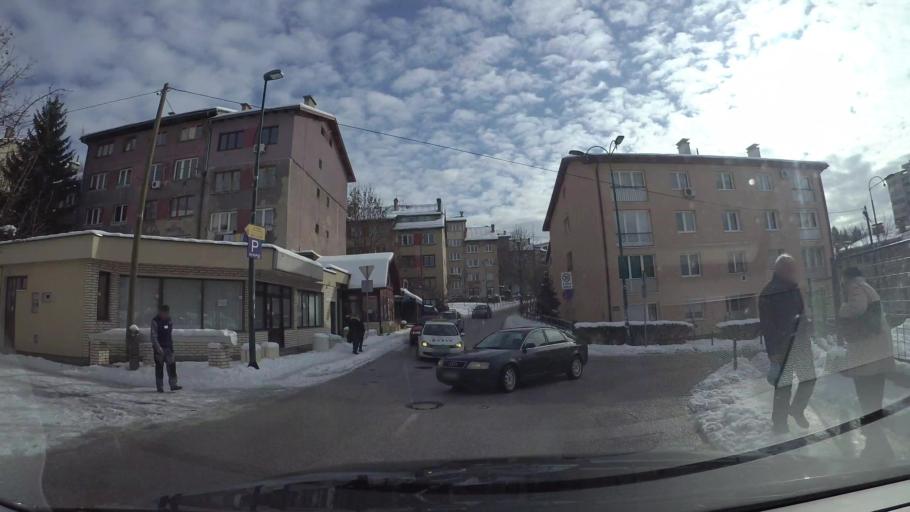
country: BA
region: Federation of Bosnia and Herzegovina
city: Kobilja Glava
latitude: 43.8690
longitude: 18.4190
